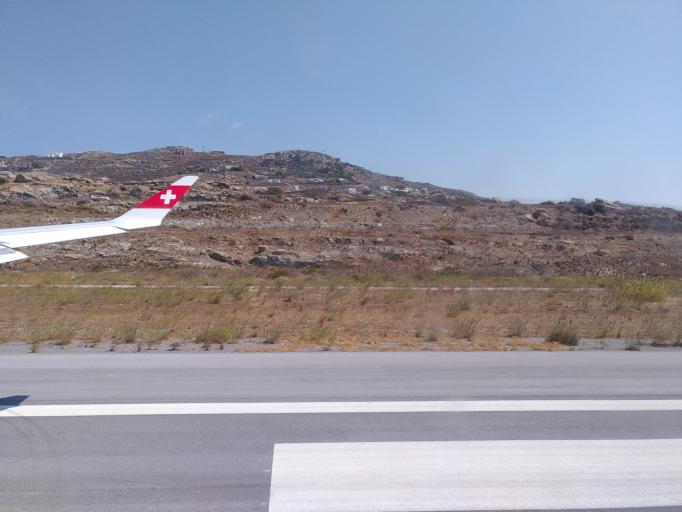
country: GR
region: South Aegean
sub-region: Nomos Kykladon
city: Mykonos
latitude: 37.4285
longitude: 25.3513
